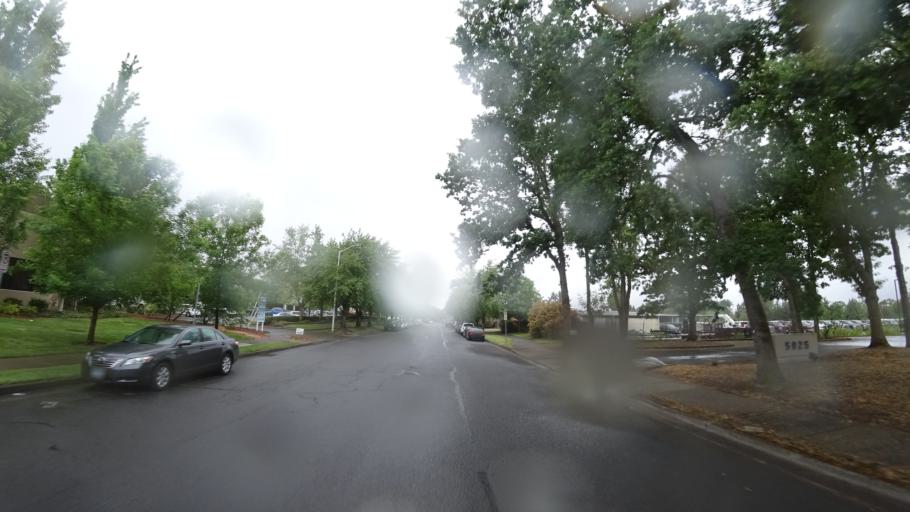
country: US
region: Oregon
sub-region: Washington County
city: Raleigh Hills
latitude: 45.4777
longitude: -122.7787
